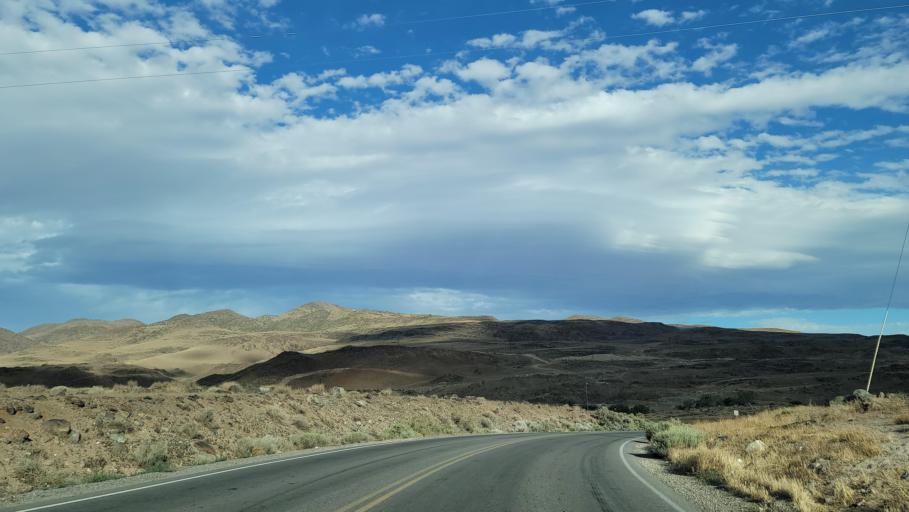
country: US
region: Nevada
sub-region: Washoe County
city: Sparks
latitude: 39.5214
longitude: -119.6230
